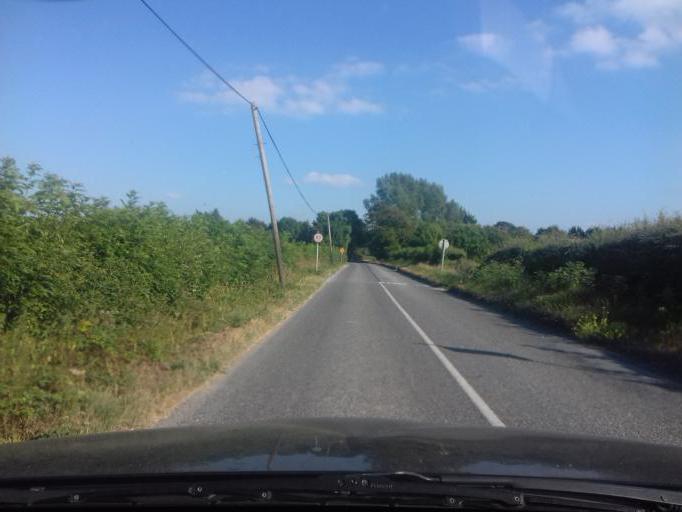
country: IE
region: Leinster
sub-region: An Mhi
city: Ashbourne
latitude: 53.4492
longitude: -6.3935
